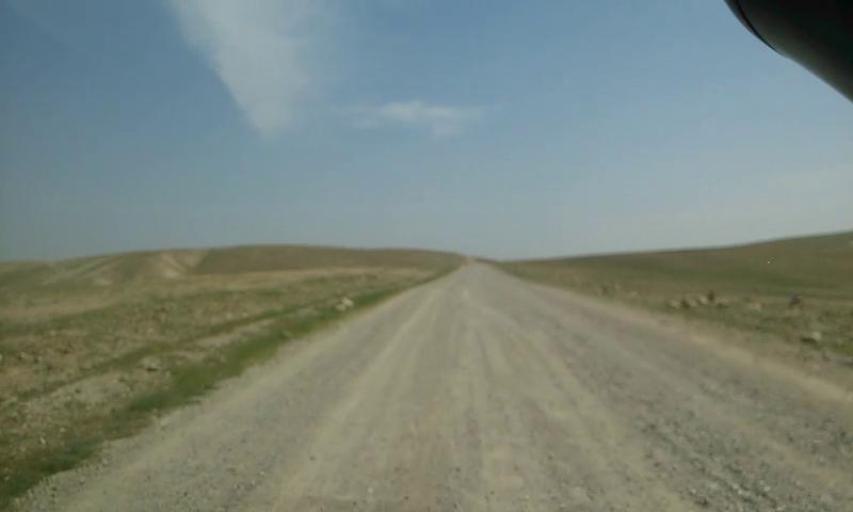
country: PS
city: `Arab ar Rashaydah
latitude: 31.5266
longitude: 35.2948
